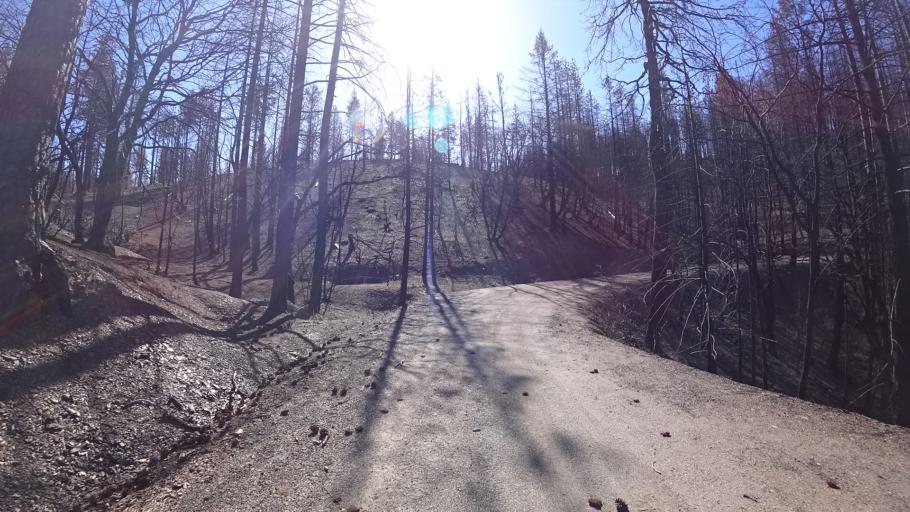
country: US
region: California
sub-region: Tehama County
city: Rancho Tehama Reserve
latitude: 39.6711
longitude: -122.7080
